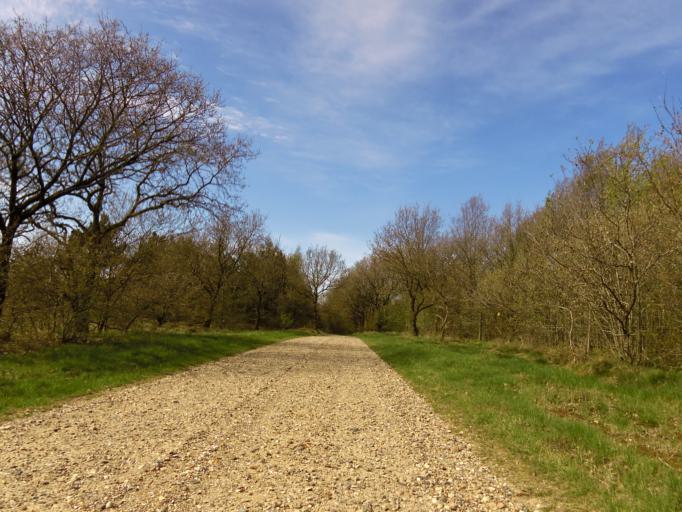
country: DK
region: Central Jutland
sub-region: Holstebro Kommune
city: Vinderup
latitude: 56.4778
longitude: 8.8730
